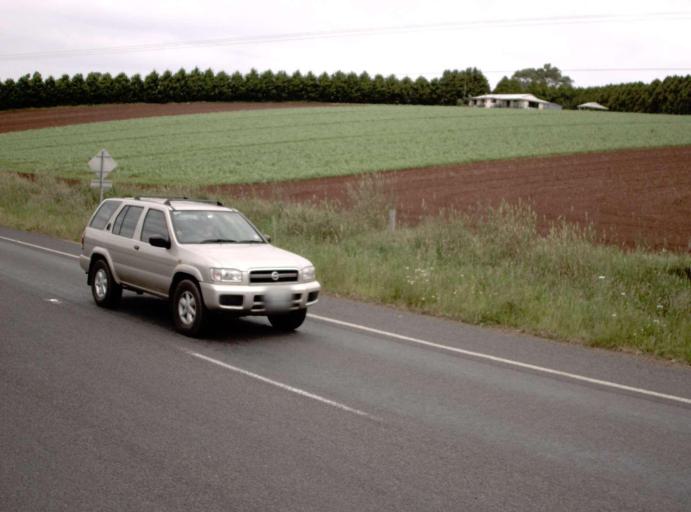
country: AU
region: Victoria
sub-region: Baw Baw
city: Warragul
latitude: -38.4617
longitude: 145.9335
